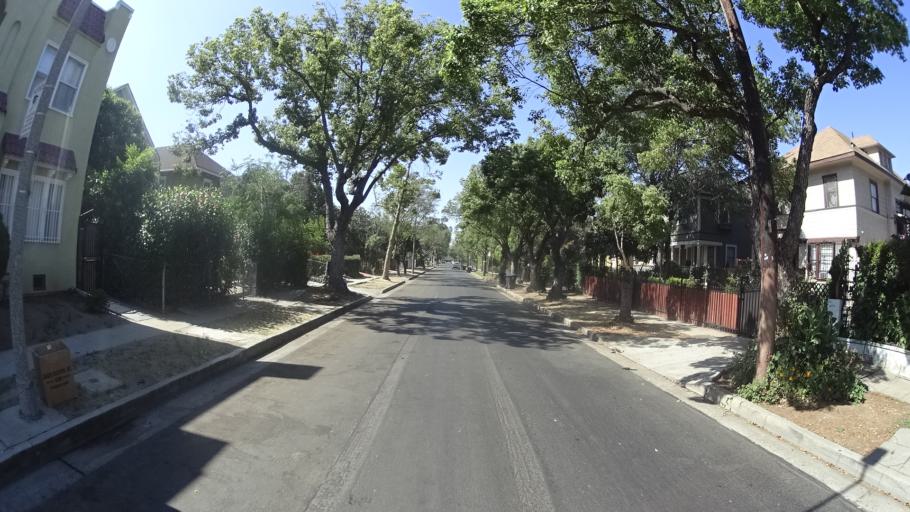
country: US
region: California
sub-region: Los Angeles County
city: Los Angeles
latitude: 34.0322
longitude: -118.2876
